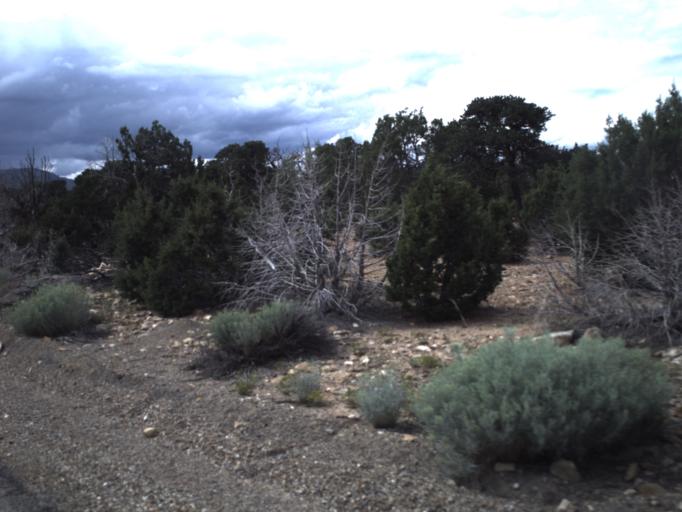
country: US
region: Utah
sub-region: Carbon County
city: Price
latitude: 39.4835
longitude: -110.9148
